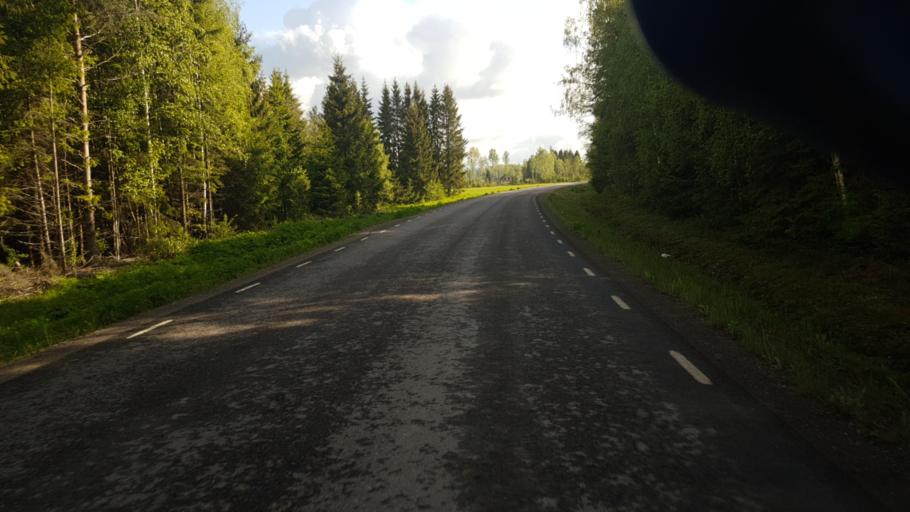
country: SE
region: Vaermland
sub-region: Eda Kommun
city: Charlottenberg
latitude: 59.7862
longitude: 12.1910
